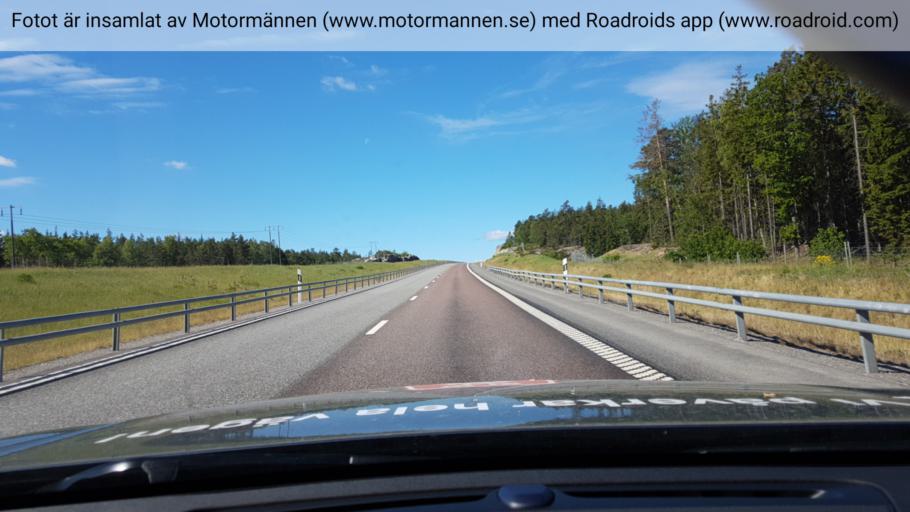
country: SE
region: Stockholm
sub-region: Nynashamns Kommun
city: Osmo
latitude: 59.0535
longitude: 18.0004
